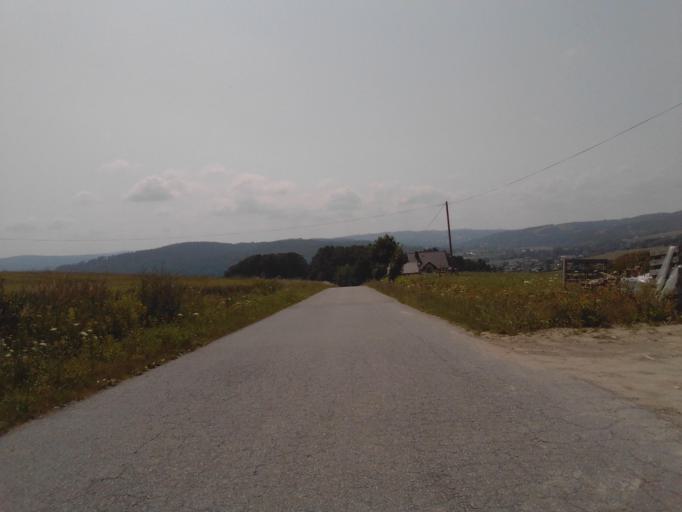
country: PL
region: Subcarpathian Voivodeship
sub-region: Powiat strzyzowski
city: Czudec
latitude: 49.9497
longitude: 21.8081
